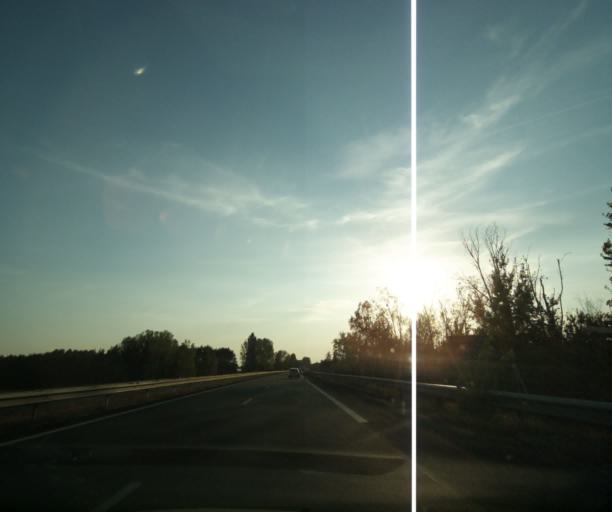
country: FR
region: Midi-Pyrenees
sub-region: Departement du Tarn-et-Garonne
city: Castelsarrasin
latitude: 44.0494
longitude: 1.0869
